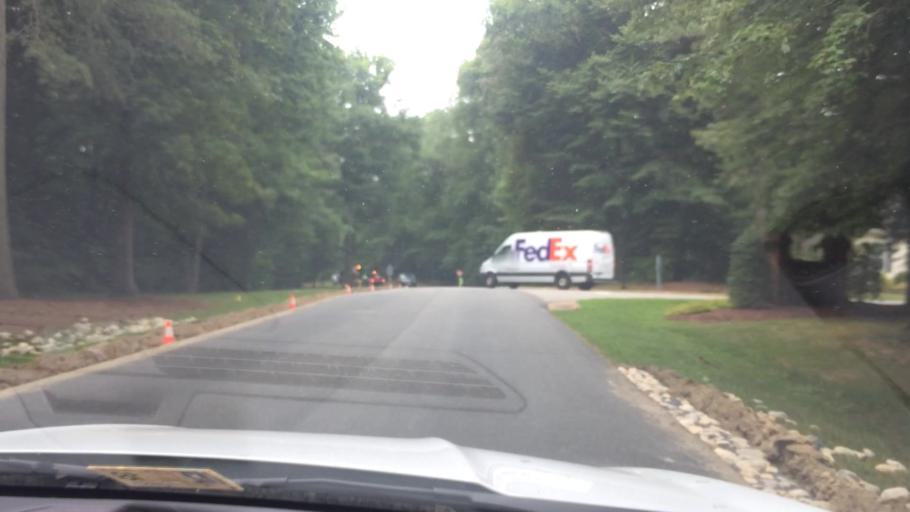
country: US
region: Virginia
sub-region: James City County
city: Williamsburg
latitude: 37.2954
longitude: -76.7953
